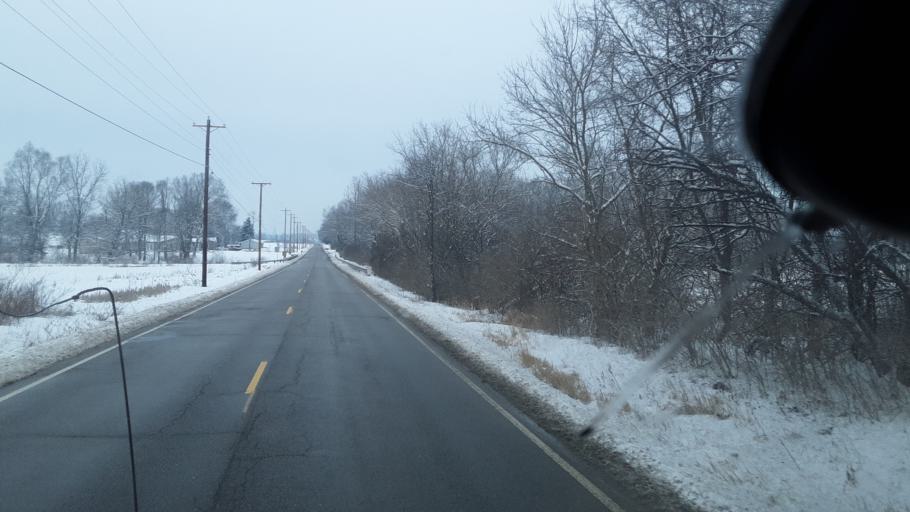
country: US
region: Ohio
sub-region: Licking County
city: Heath
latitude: 40.0065
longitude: -82.4816
